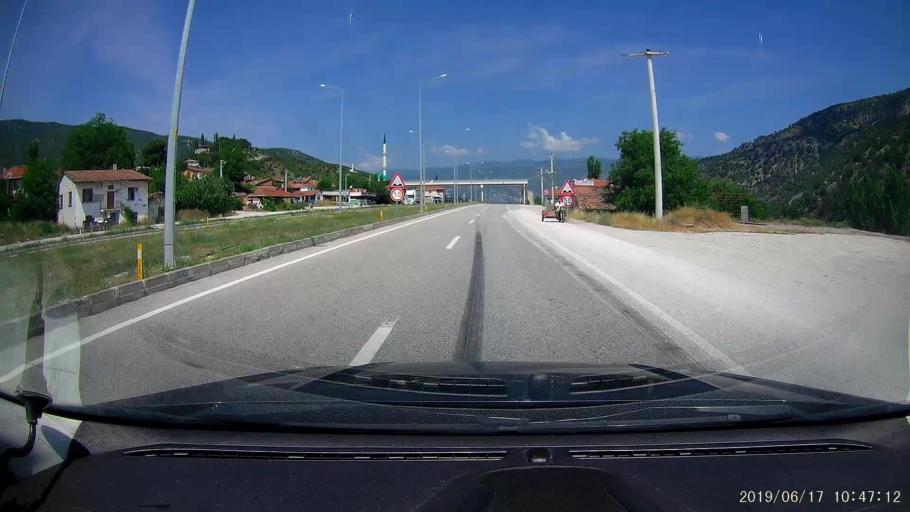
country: TR
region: Corum
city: Hacihamza
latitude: 41.0748
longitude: 34.4523
